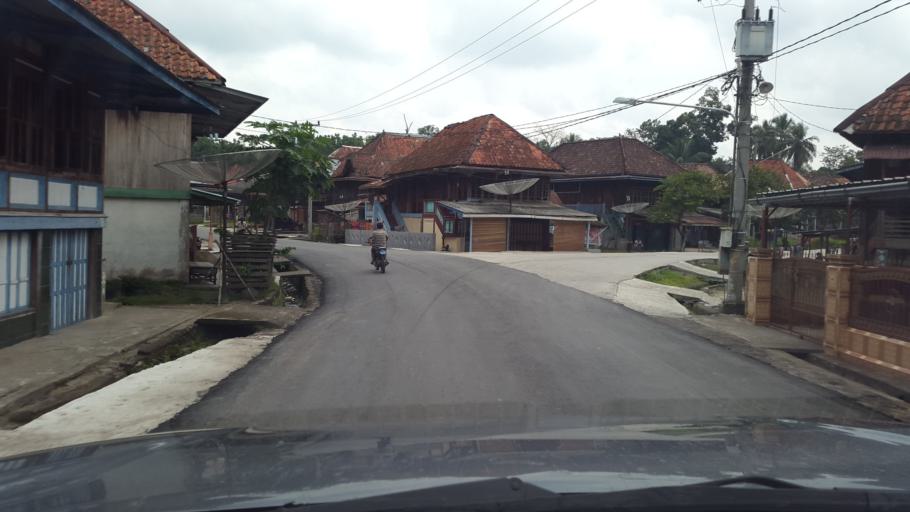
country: ID
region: South Sumatra
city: Gunungmenang
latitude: -3.1660
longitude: 103.9378
